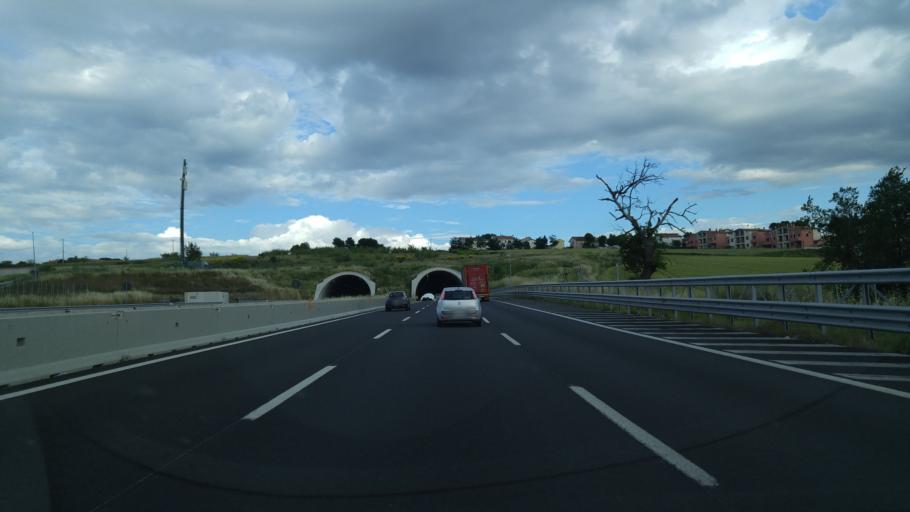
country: IT
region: Emilia-Romagna
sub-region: Provincia di Rimini
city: Riccione
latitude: 43.9804
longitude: 12.6529
